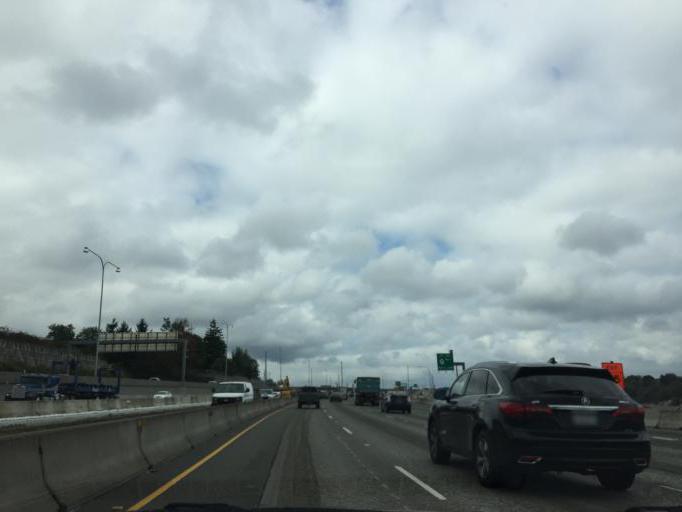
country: US
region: Washington
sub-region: Pierce County
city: Tacoma
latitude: 47.2302
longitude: -122.4484
